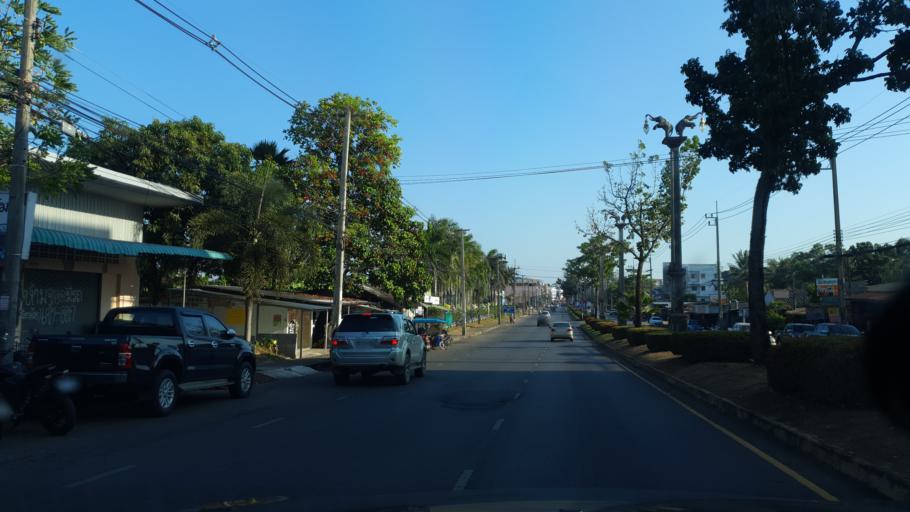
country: TH
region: Krabi
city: Krabi
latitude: 8.0726
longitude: 98.9116
